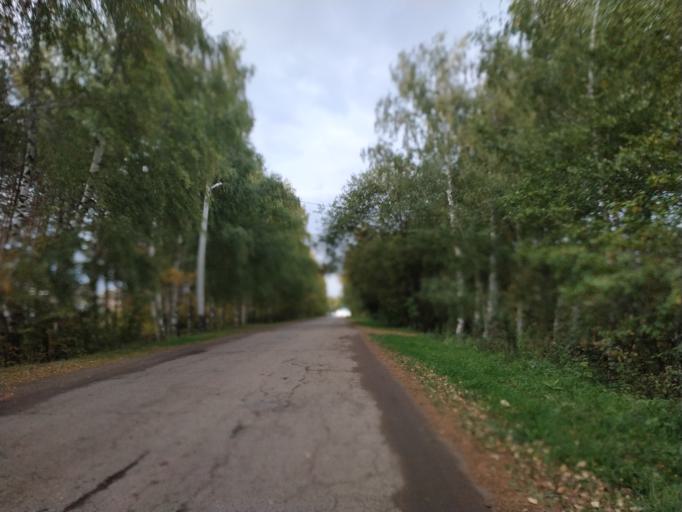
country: RU
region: Chuvashia
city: Ishley
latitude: 56.1295
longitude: 47.0894
